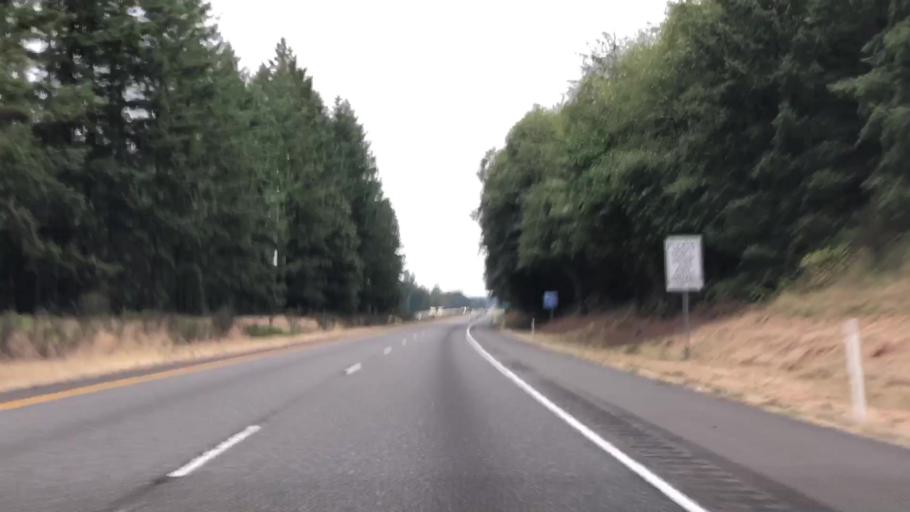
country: US
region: Washington
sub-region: Kitsap County
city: Burley
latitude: 47.4245
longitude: -122.6234
